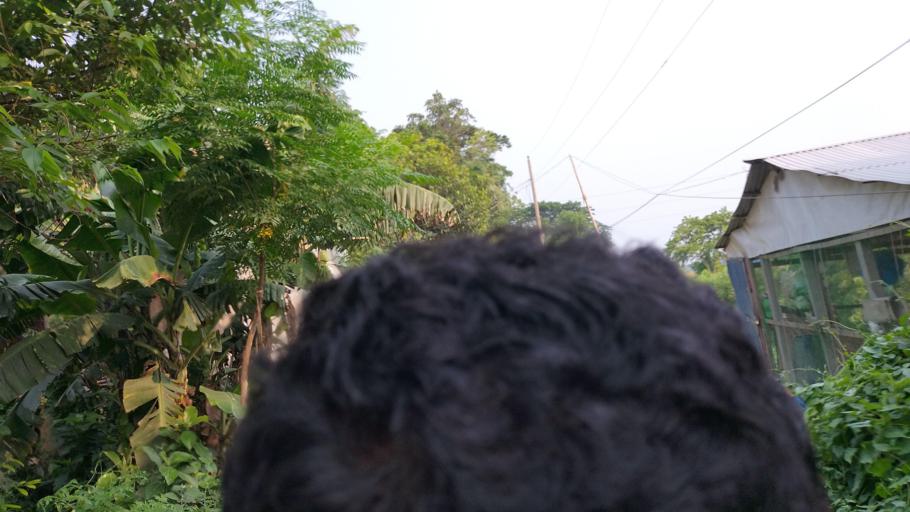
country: BD
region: Dhaka
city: Azimpur
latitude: 23.6690
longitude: 90.3149
